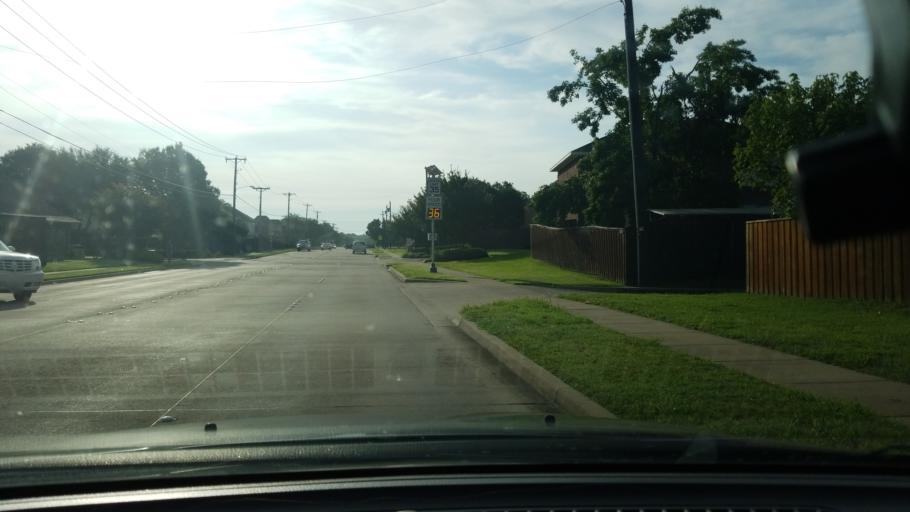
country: US
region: Texas
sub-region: Dallas County
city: Mesquite
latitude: 32.7976
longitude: -96.6063
